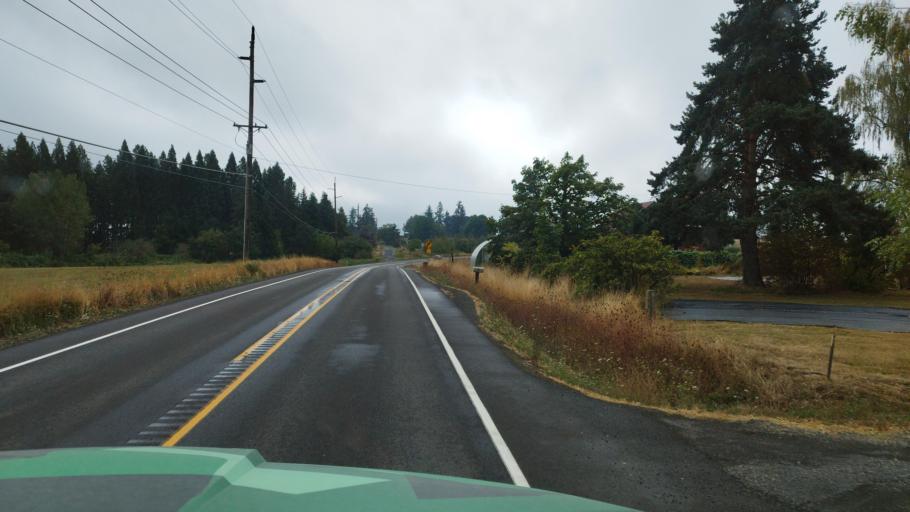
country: US
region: Oregon
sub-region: Yamhill County
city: Yamhill
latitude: 45.3209
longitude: -123.1771
